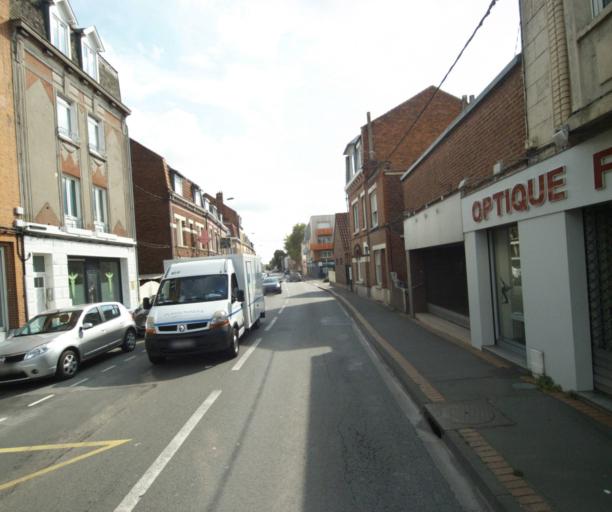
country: FR
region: Nord-Pas-de-Calais
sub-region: Departement du Nord
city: Perenchies
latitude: 50.6670
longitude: 2.9736
